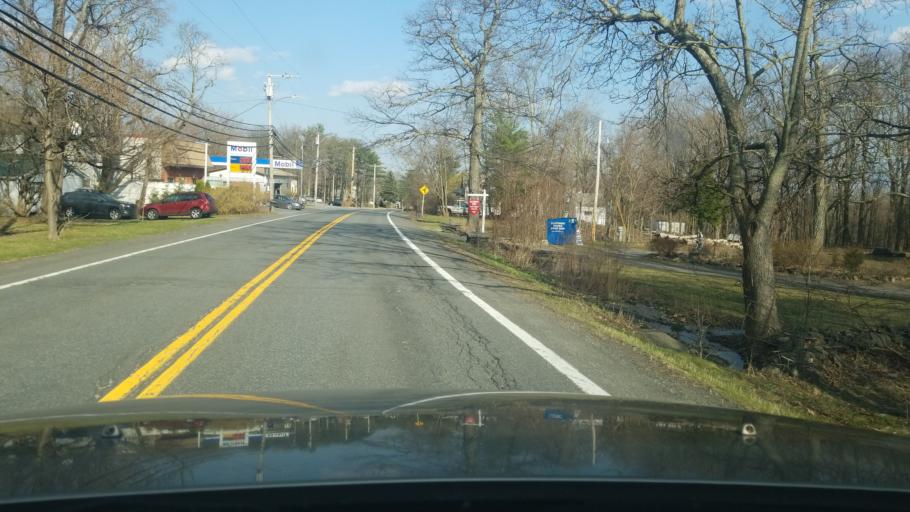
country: US
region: New York
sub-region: Greene County
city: Palenville
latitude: 42.1753
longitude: -74.0258
